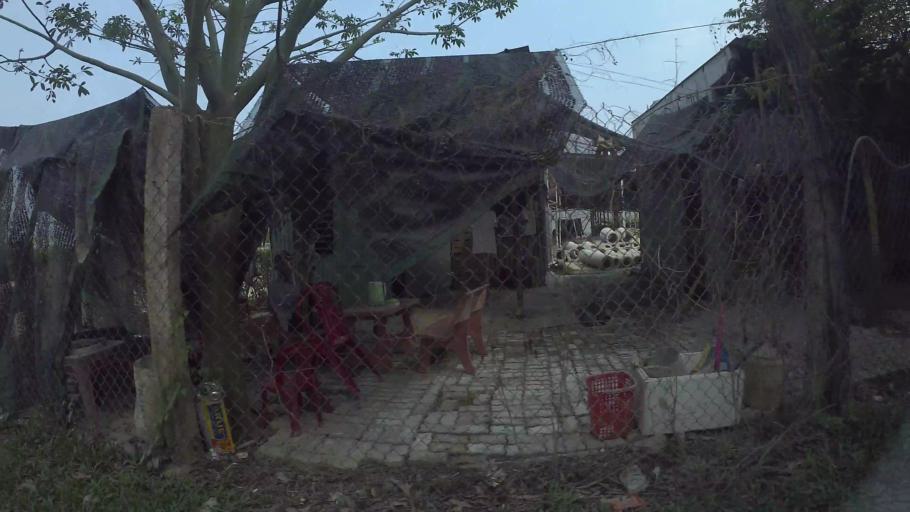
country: VN
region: Da Nang
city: Lien Chieu
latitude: 16.0453
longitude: 108.1463
